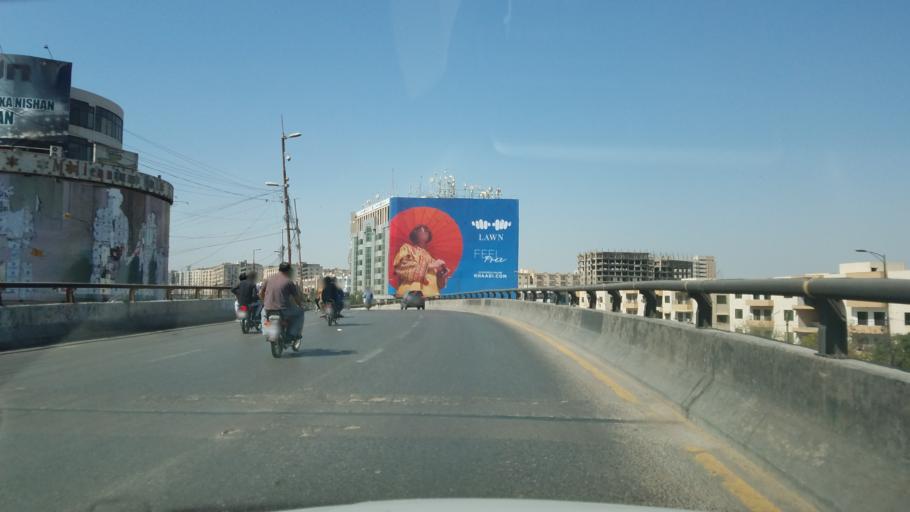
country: PK
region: Sindh
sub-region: Karachi District
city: Karachi
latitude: 24.9006
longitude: 67.1163
